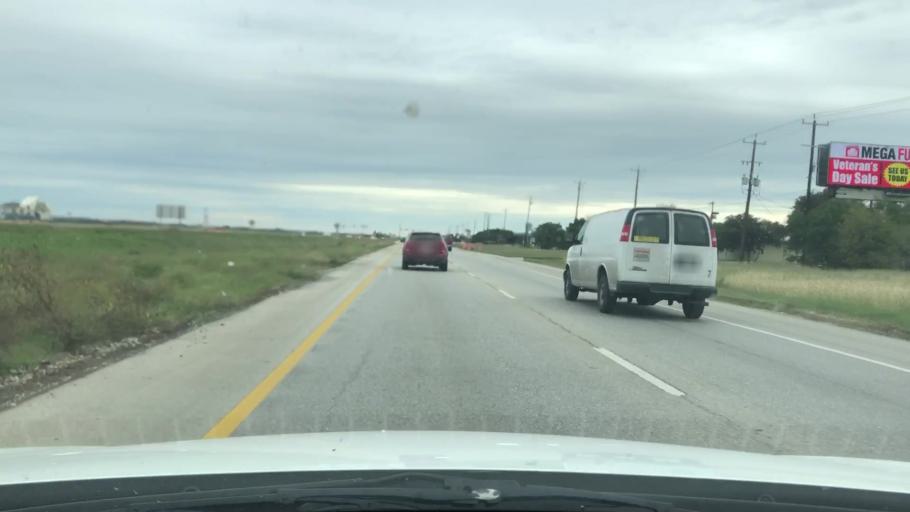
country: US
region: Texas
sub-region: Bexar County
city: Converse
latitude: 29.5244
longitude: -98.2962
